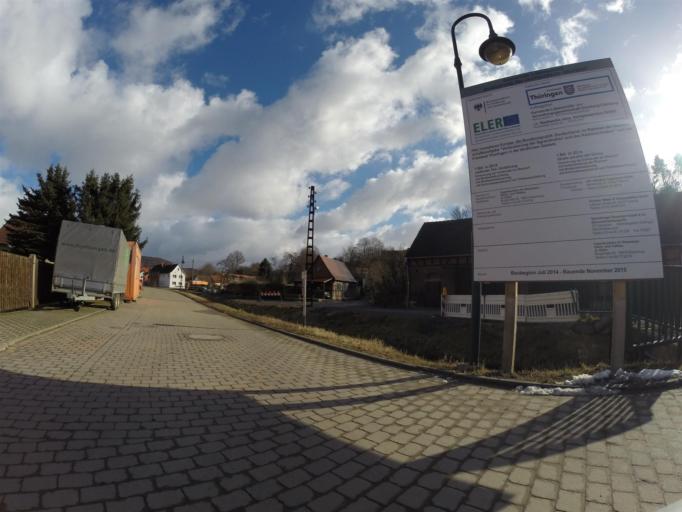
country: DE
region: Thuringia
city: Loberschutz
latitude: 50.9648
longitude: 11.7005
